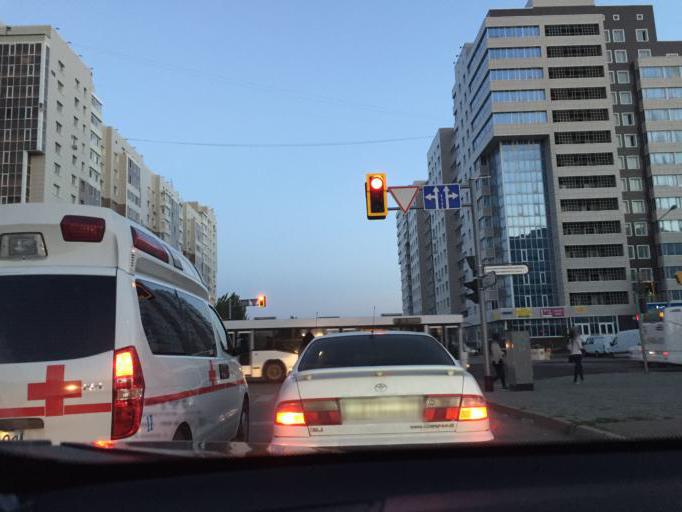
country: KZ
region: Astana Qalasy
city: Astana
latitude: 51.1414
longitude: 71.4819
